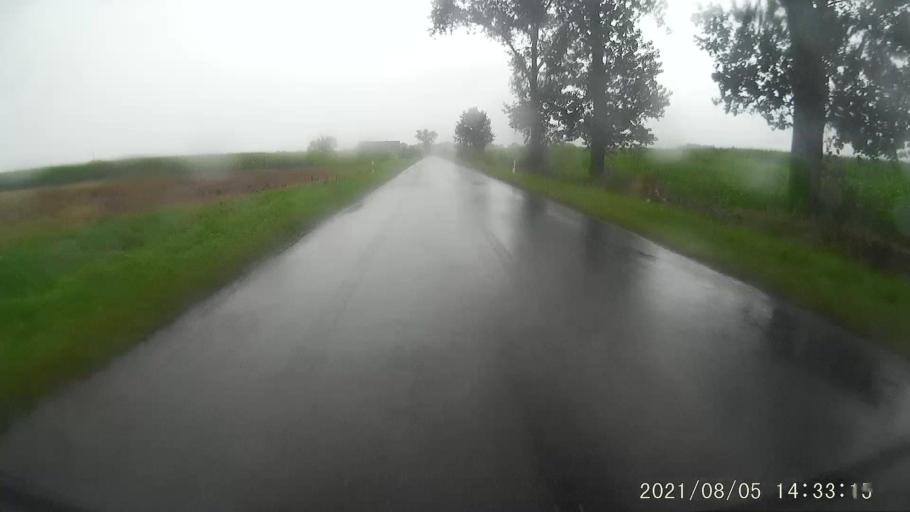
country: PL
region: Opole Voivodeship
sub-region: Powiat nyski
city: Korfantow
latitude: 50.4683
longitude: 17.5405
